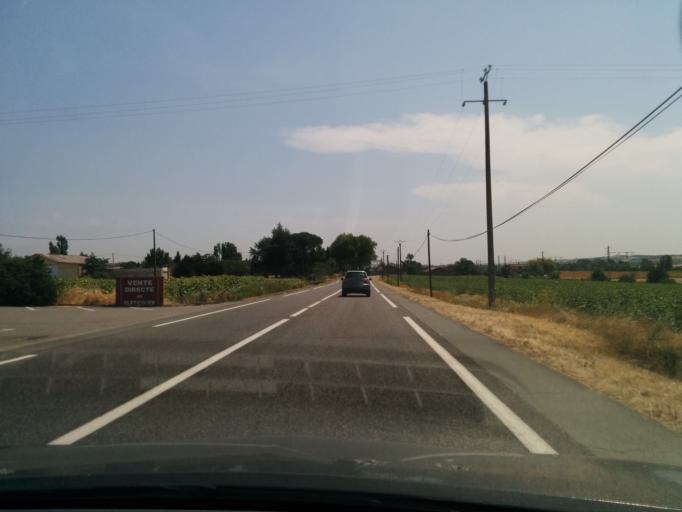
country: FR
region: Midi-Pyrenees
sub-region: Departement de la Haute-Garonne
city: Villenouvelle
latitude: 43.4239
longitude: 1.6822
